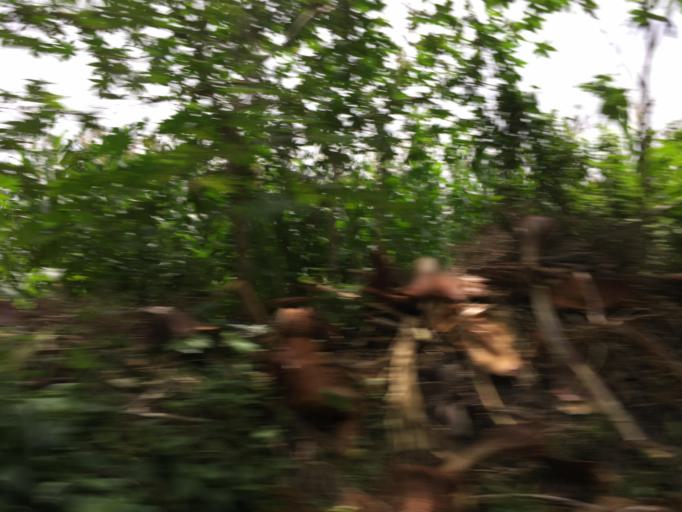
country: GT
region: Guatemala
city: Villa Canales
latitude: 14.4307
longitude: -90.5587
